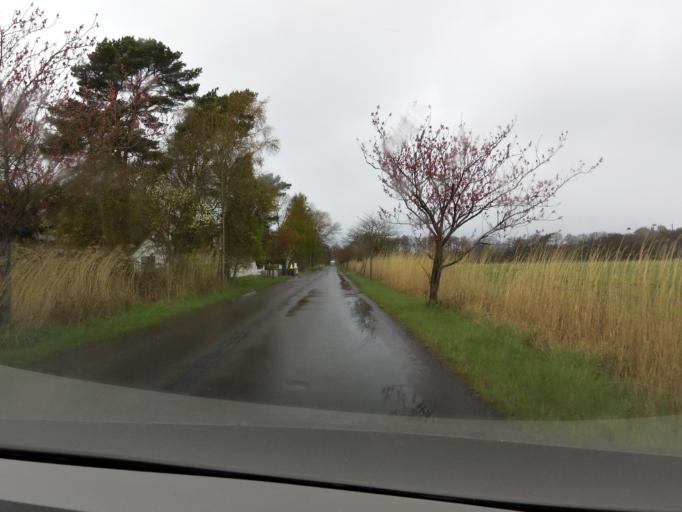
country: DE
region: Mecklenburg-Vorpommern
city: Zingst
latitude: 54.4322
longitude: 12.7334
